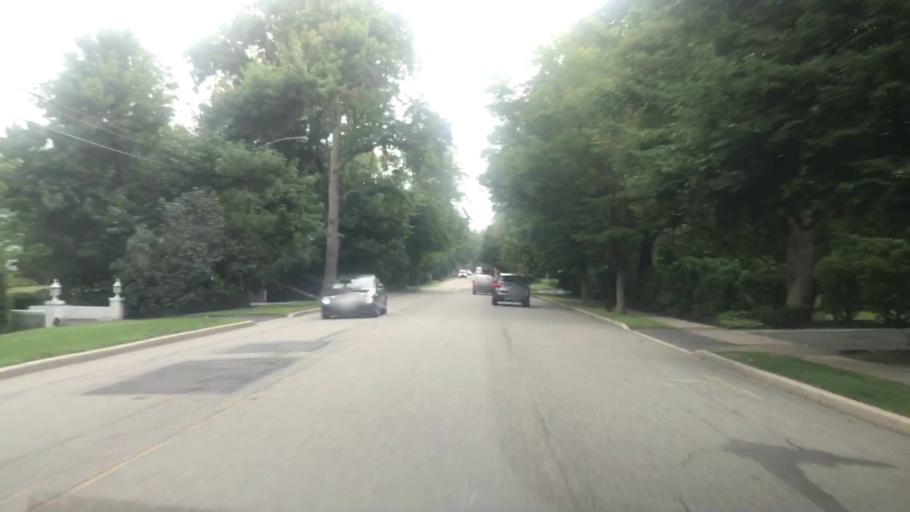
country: US
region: New Jersey
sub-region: Bergen County
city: Englewood
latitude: 40.8799
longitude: -73.9748
